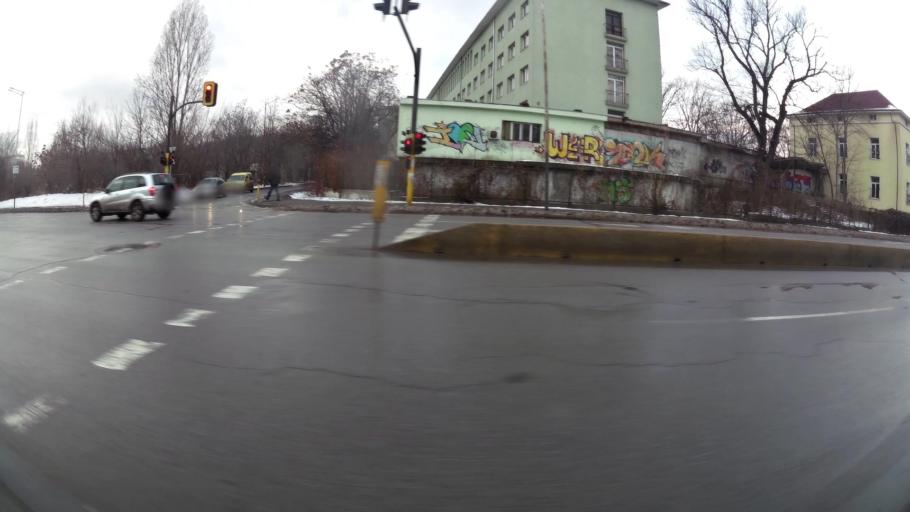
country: BG
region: Sofia-Capital
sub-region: Stolichna Obshtina
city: Sofia
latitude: 42.7041
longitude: 23.2932
